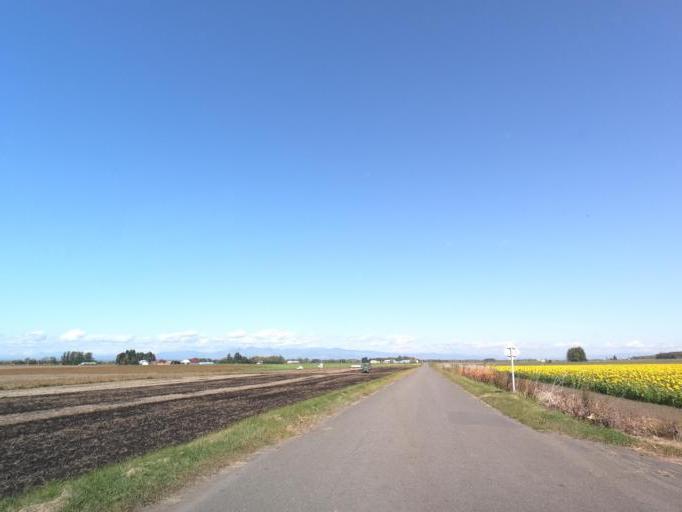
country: JP
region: Hokkaido
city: Otofuke
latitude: 43.0171
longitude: 143.2682
